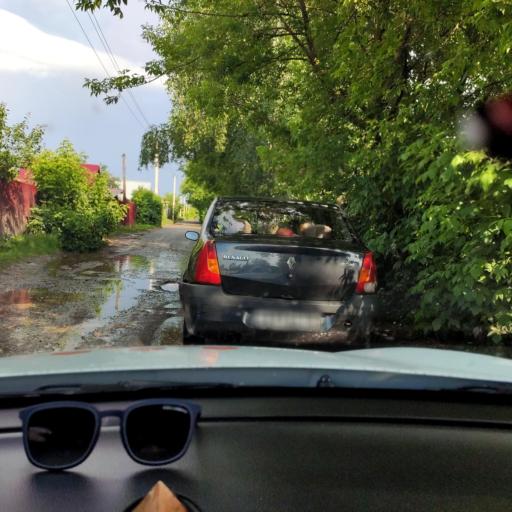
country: RU
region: Tatarstan
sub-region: Zelenodol'skiy Rayon
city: Vasil'yevo
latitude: 55.8282
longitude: 48.7503
